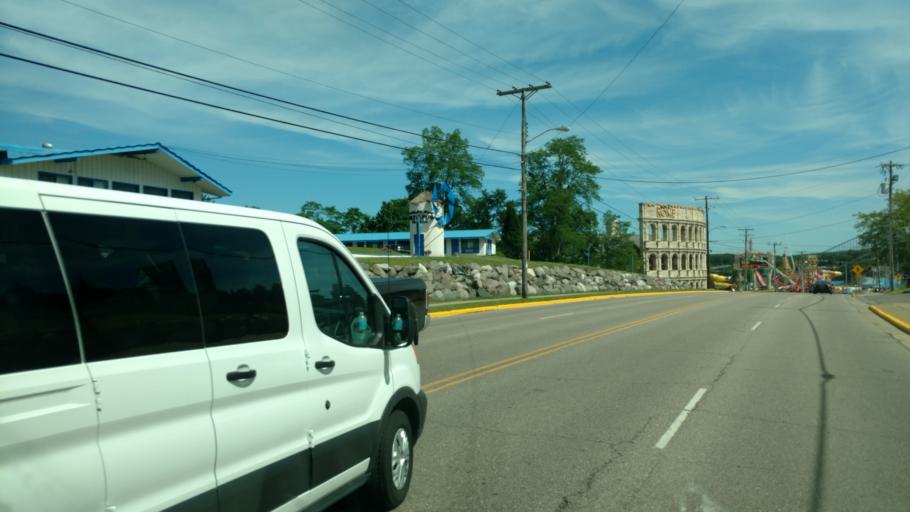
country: US
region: Wisconsin
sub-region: Sauk County
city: Lake Delton
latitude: 43.6090
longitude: -89.7913
